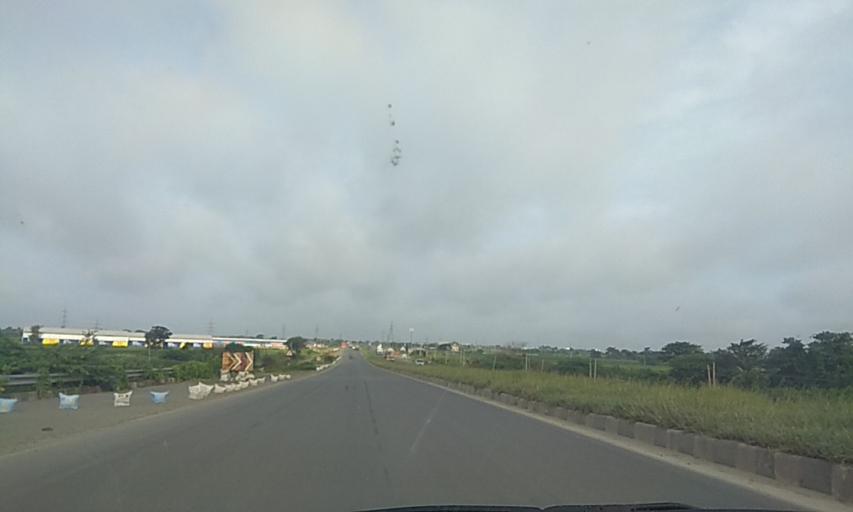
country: IN
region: Karnataka
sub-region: Haveri
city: Haveri
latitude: 14.7750
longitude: 75.4030
